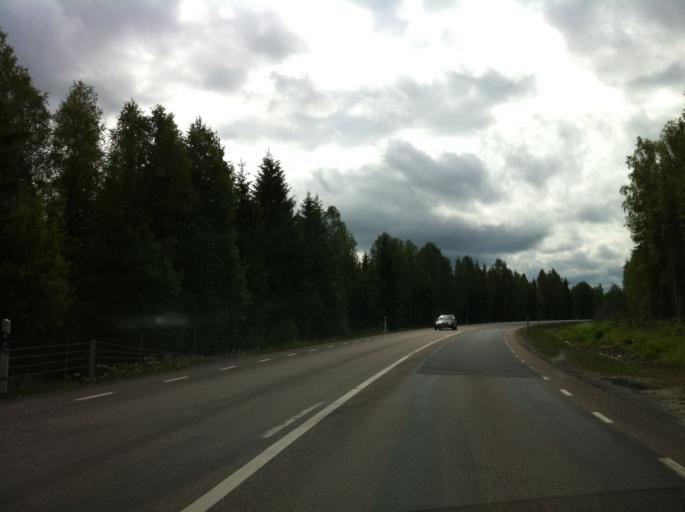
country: SE
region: Vaermland
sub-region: Sunne Kommun
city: Sunne
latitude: 59.7649
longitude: 13.1091
